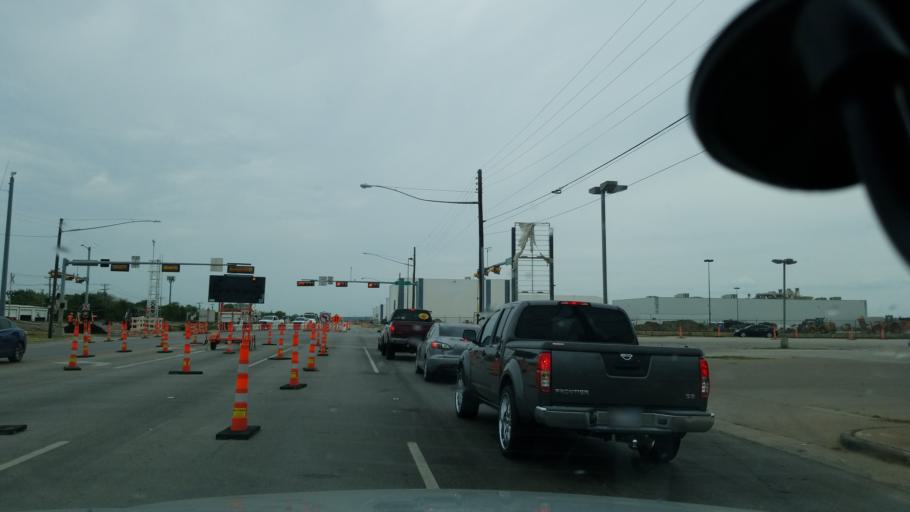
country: US
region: Texas
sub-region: Dallas County
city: Grand Prairie
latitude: 32.7450
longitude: -96.9884
